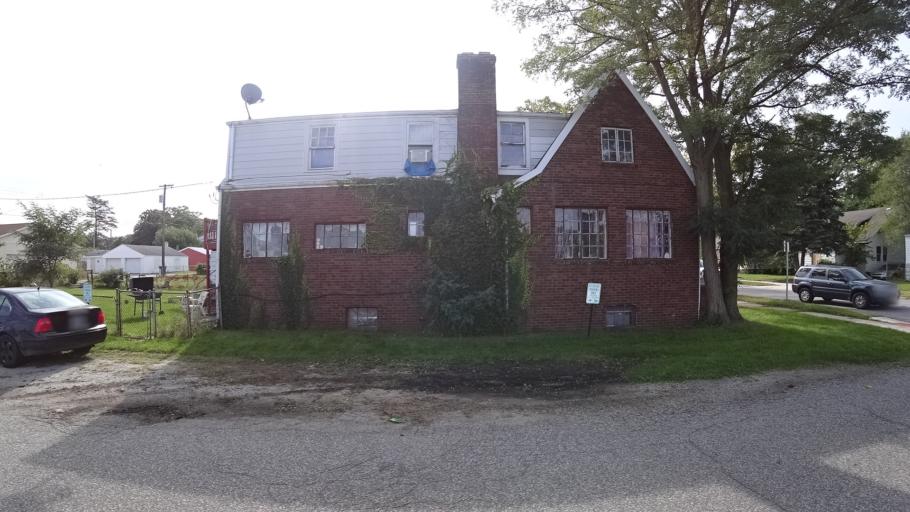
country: US
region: Indiana
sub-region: LaPorte County
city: Trail Creek
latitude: 41.7131
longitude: -86.8695
